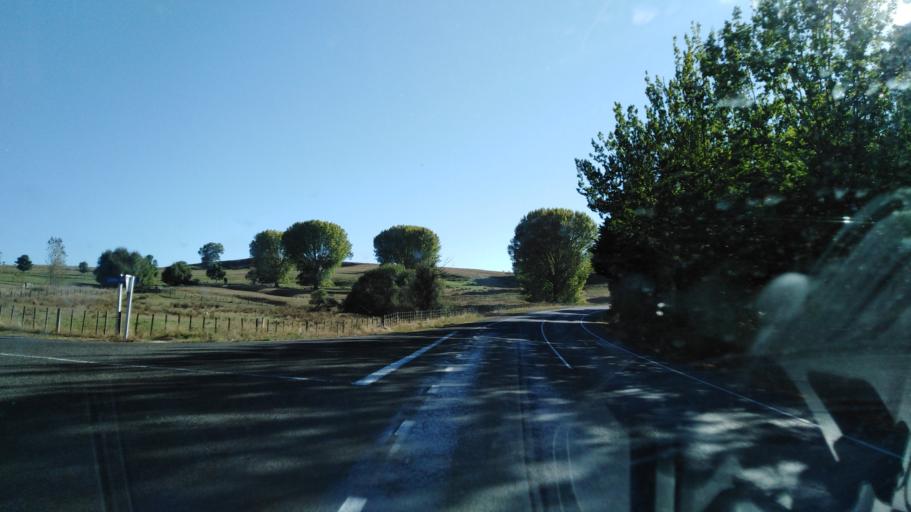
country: NZ
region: Manawatu-Wanganui
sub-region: Ruapehu District
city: Waiouru
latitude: -39.7432
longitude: 175.8354
